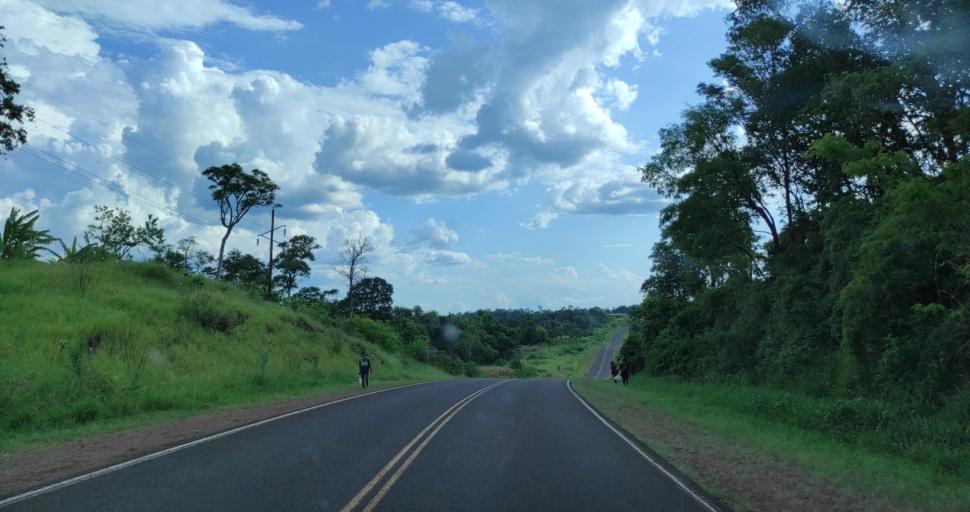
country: AR
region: Misiones
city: San Vicente
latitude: -26.3455
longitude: -54.1828
